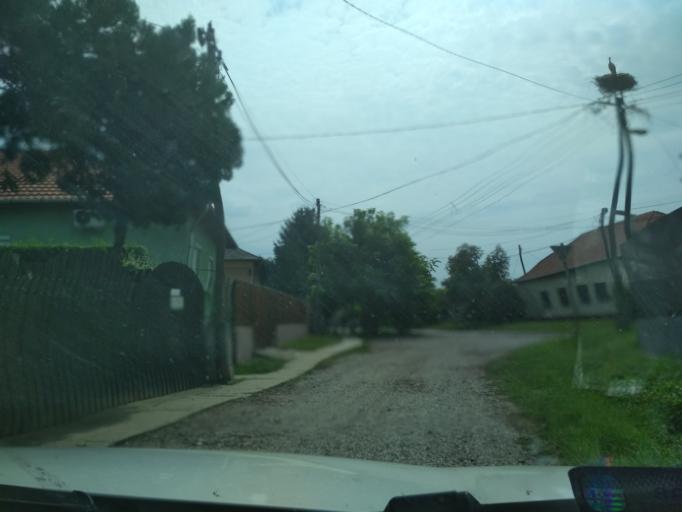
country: HU
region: Jasz-Nagykun-Szolnok
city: Tiszafured
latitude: 47.6146
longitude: 20.7682
